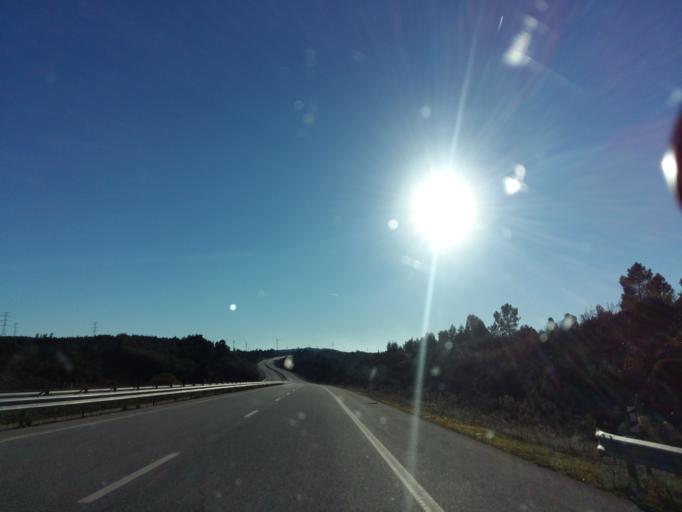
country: PT
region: Castelo Branco
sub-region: Castelo Branco
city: Castelo Branco
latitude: 39.8037
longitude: -7.5573
